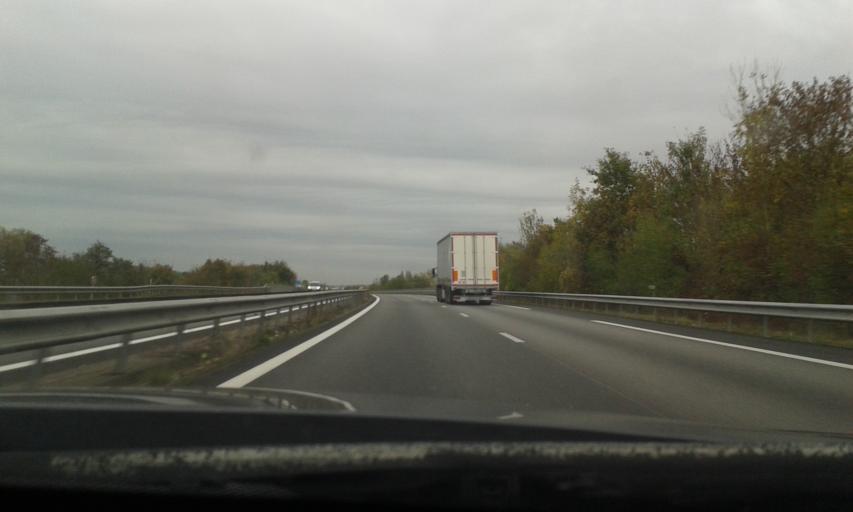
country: FR
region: Haute-Normandie
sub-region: Departement de l'Eure
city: Louviers
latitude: 49.2326
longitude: 1.1850
